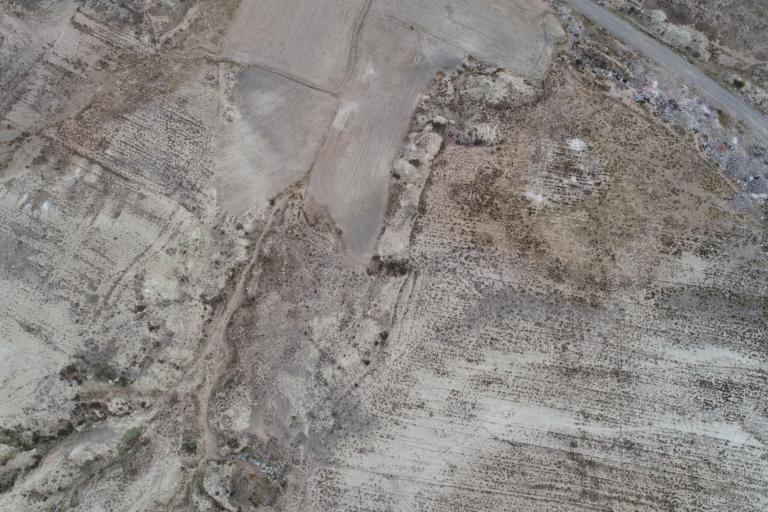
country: BO
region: La Paz
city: Achacachi
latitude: -16.0439
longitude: -68.6945
